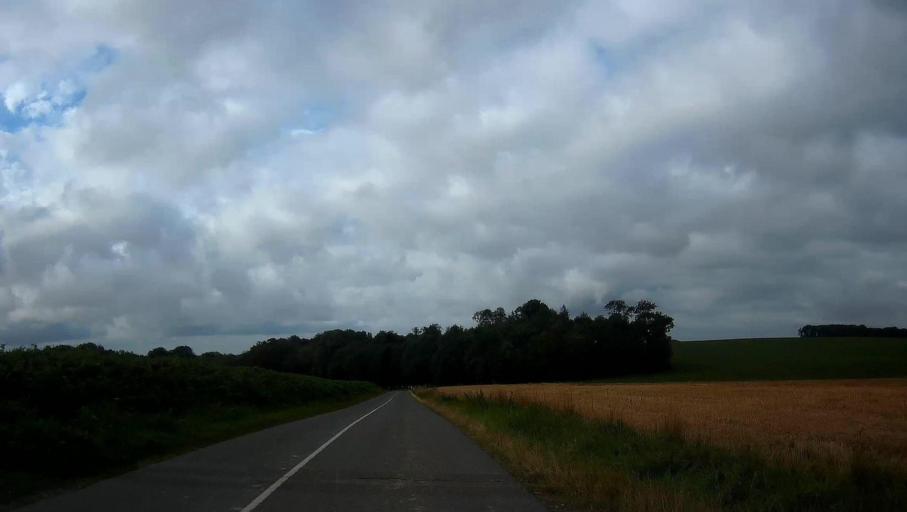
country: FR
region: Champagne-Ardenne
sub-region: Departement des Ardennes
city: Chateau-Porcien
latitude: 49.6220
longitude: 4.2339
